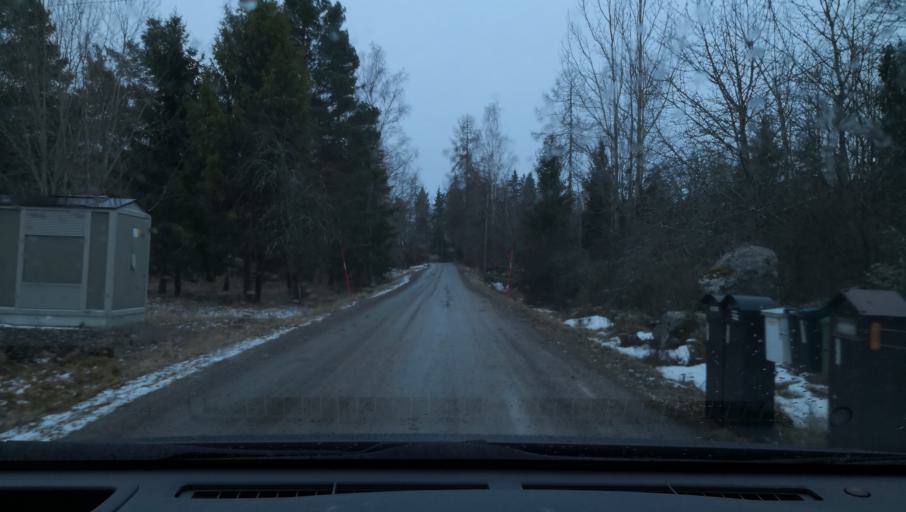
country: SE
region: Uppsala
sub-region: Enkopings Kommun
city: Hummelsta
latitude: 59.4601
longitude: 16.8258
